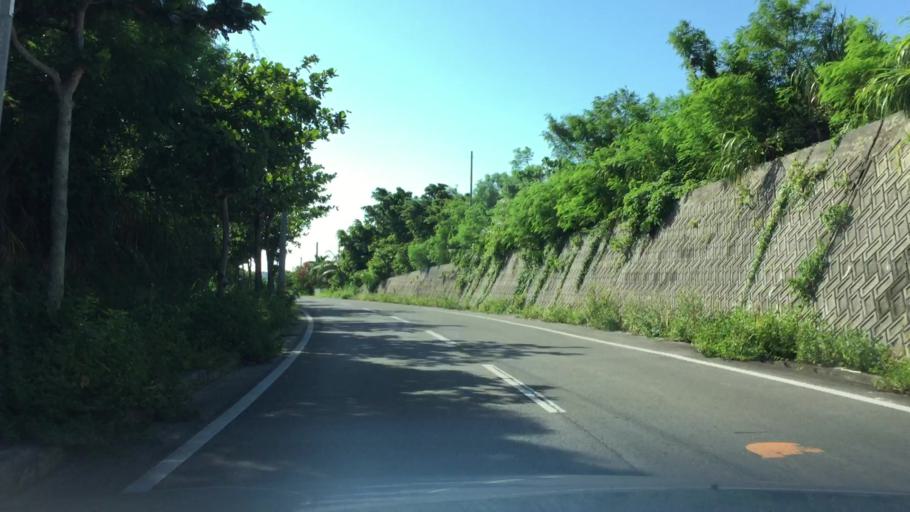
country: JP
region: Okinawa
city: Ishigaki
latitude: 24.4461
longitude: 124.1723
